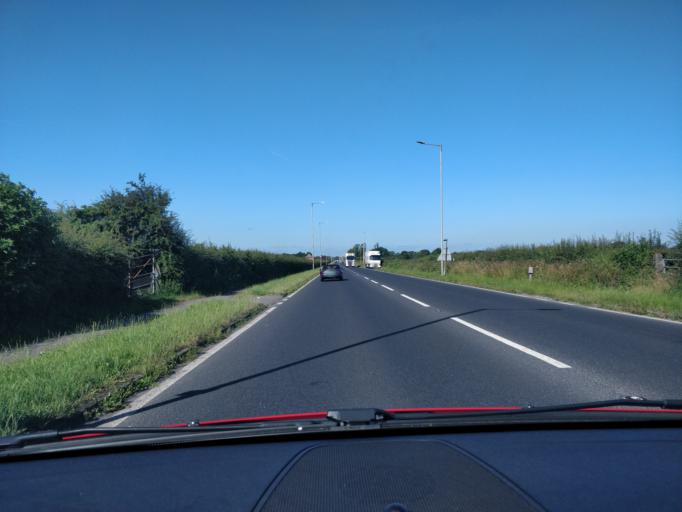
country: GB
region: England
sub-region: Lancashire
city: Tarleton
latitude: 53.6730
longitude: -2.8334
